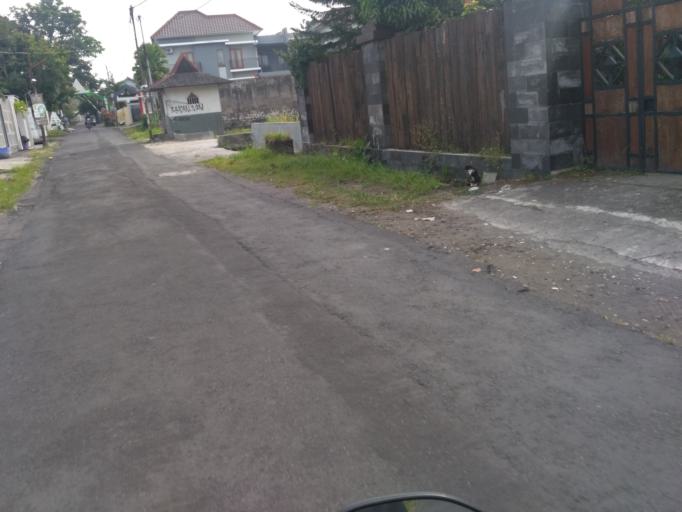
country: ID
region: Daerah Istimewa Yogyakarta
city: Melati
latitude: -7.7347
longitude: 110.3885
